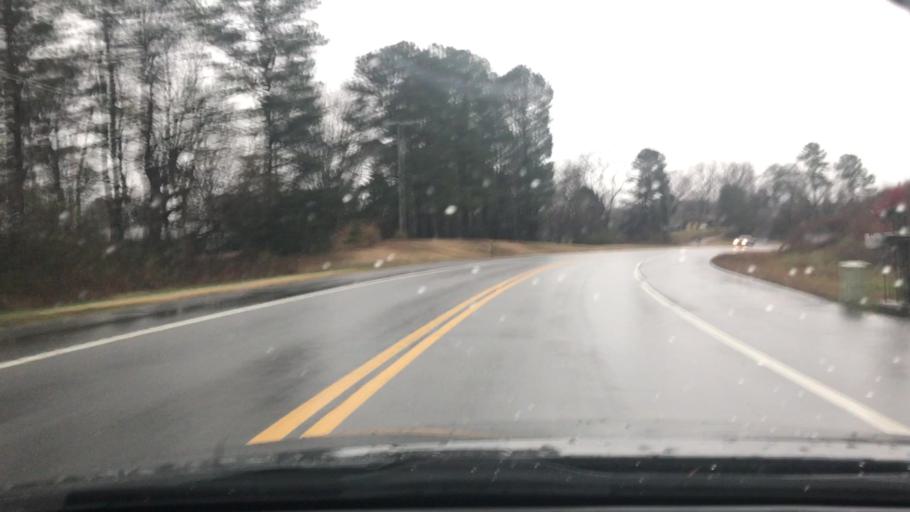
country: US
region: Tennessee
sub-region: Cheatham County
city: Ashland City
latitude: 36.2883
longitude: -87.1484
